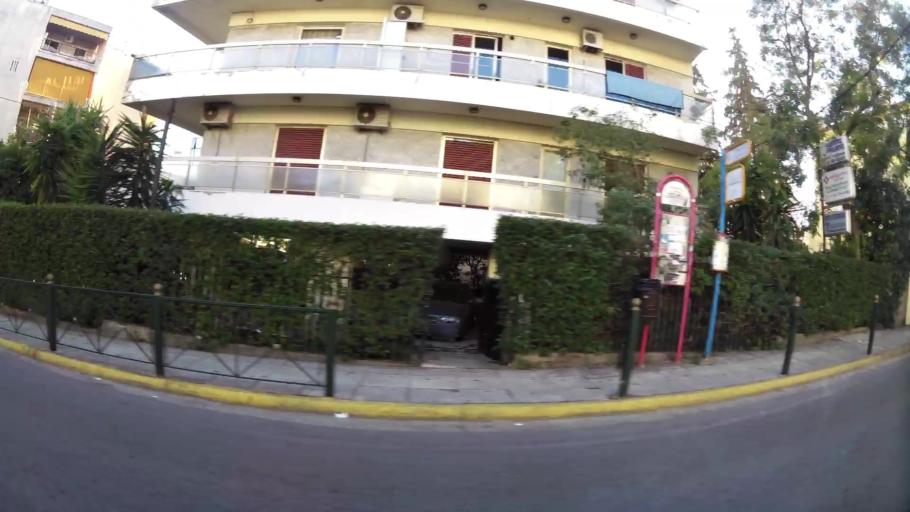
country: GR
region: Attica
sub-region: Nomarchia Athinas
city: Marousi
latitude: 38.0571
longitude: 23.8036
